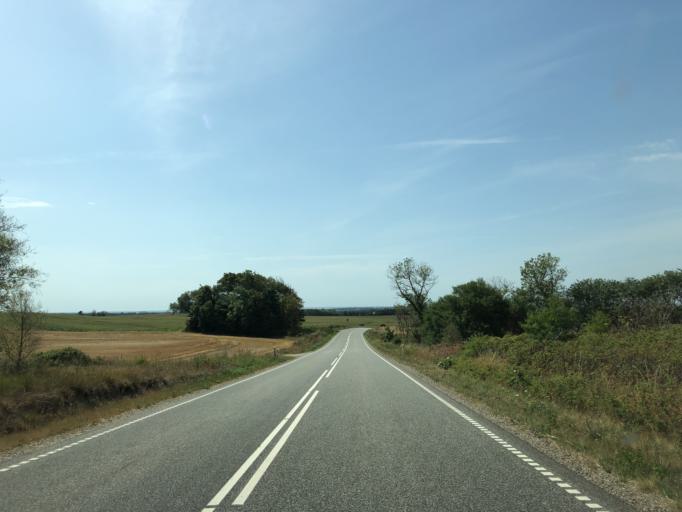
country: DK
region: Central Jutland
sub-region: Ringkobing-Skjern Kommune
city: Skjern
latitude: 56.0278
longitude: 8.4407
